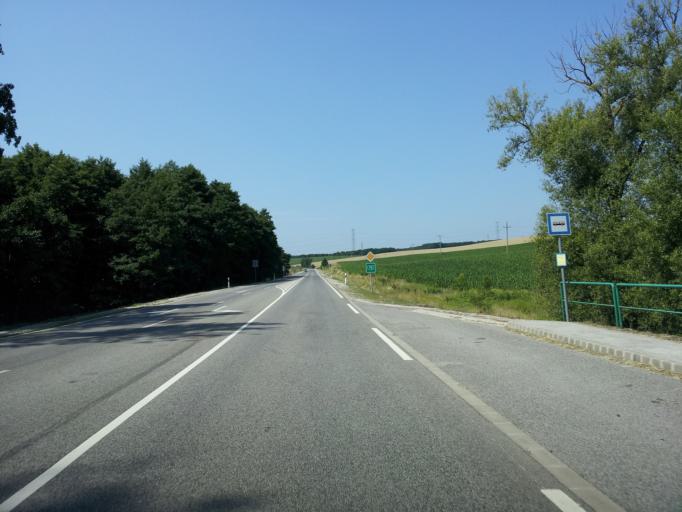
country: HU
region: Zala
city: Pacsa
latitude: 46.8349
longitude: 17.0272
